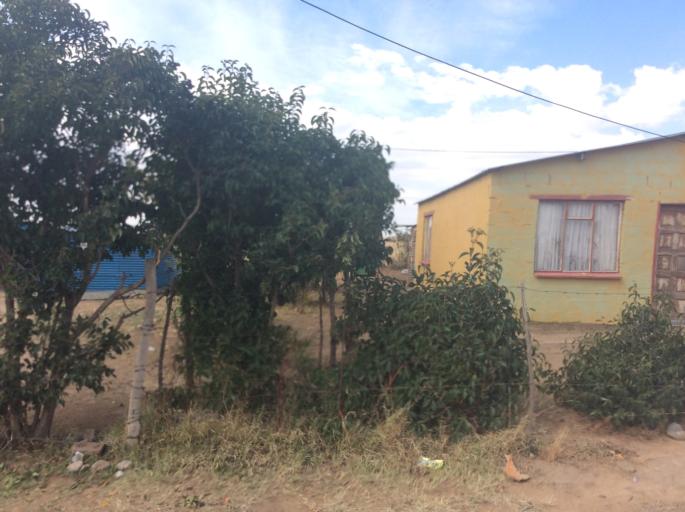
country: ZA
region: Orange Free State
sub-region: Xhariep District Municipality
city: Dewetsdorp
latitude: -29.5797
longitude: 26.6914
